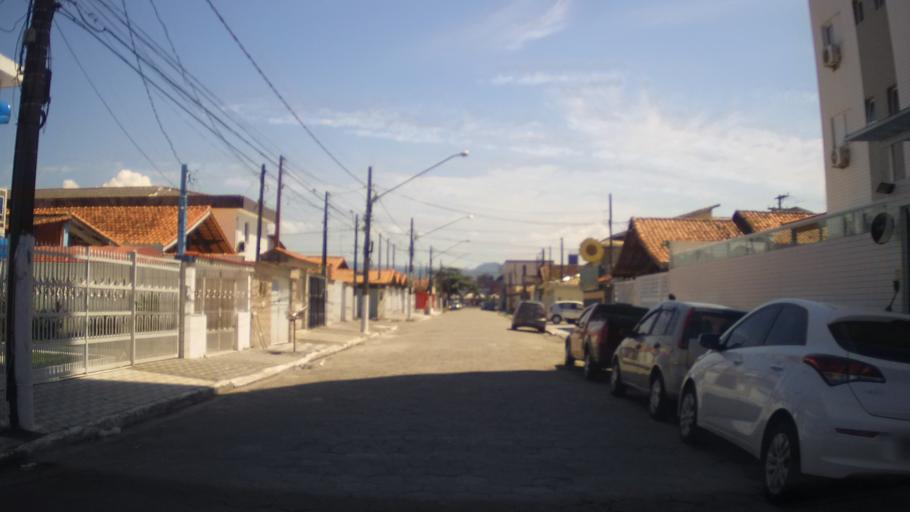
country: BR
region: Sao Paulo
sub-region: Praia Grande
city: Praia Grande
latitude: -24.0105
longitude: -46.4331
